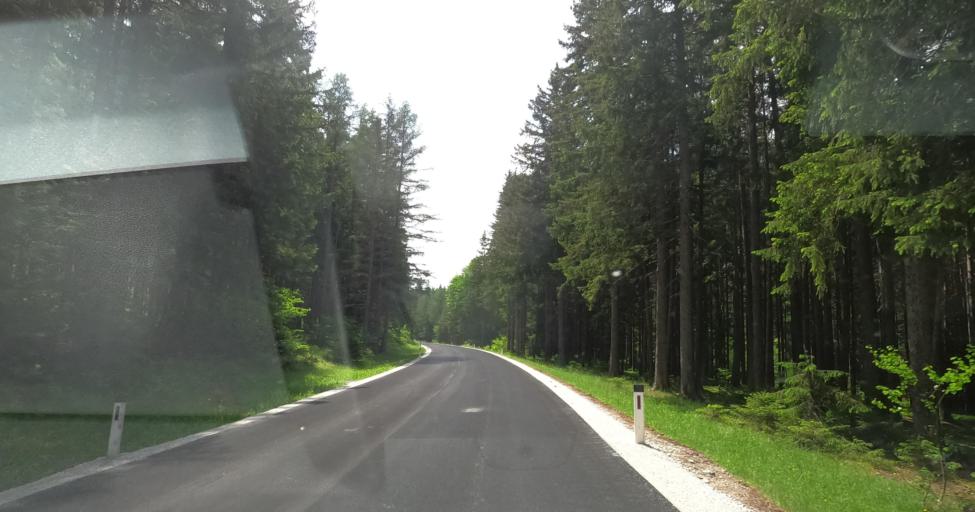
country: AT
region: Tyrol
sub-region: Politischer Bezirk Innsbruck Land
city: Patsch
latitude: 47.2206
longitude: 11.4221
